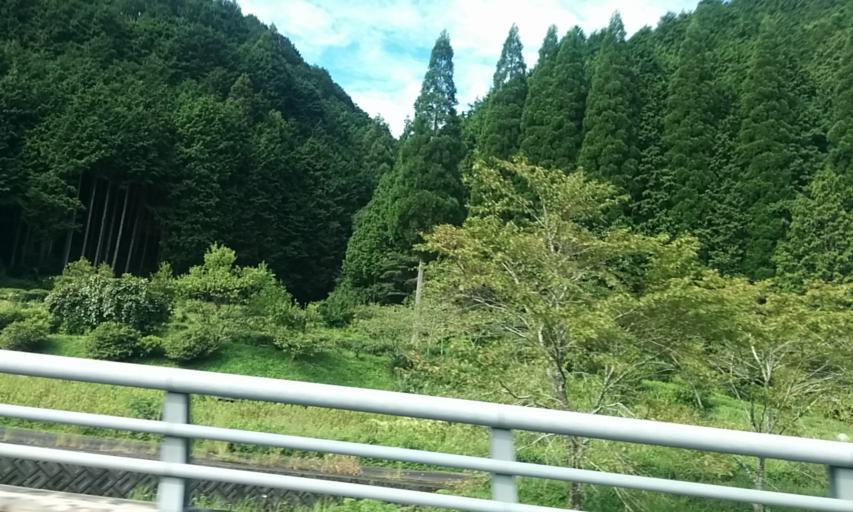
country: JP
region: Gifu
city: Minokamo
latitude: 35.5805
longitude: 137.0875
